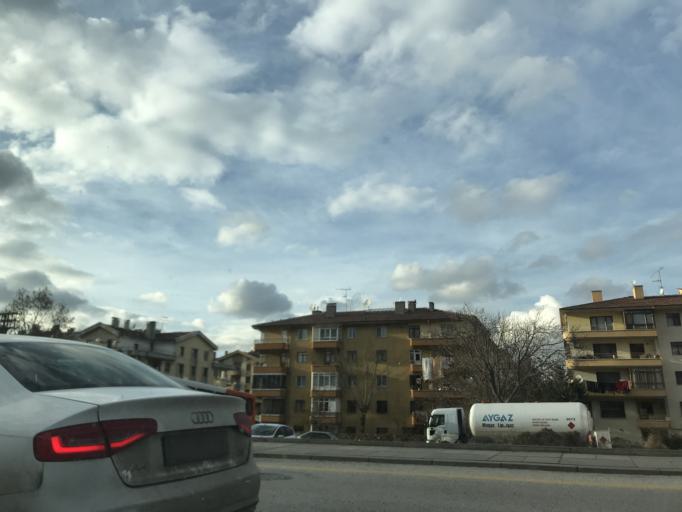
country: TR
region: Ankara
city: Mamak
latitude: 39.9833
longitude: 32.8874
